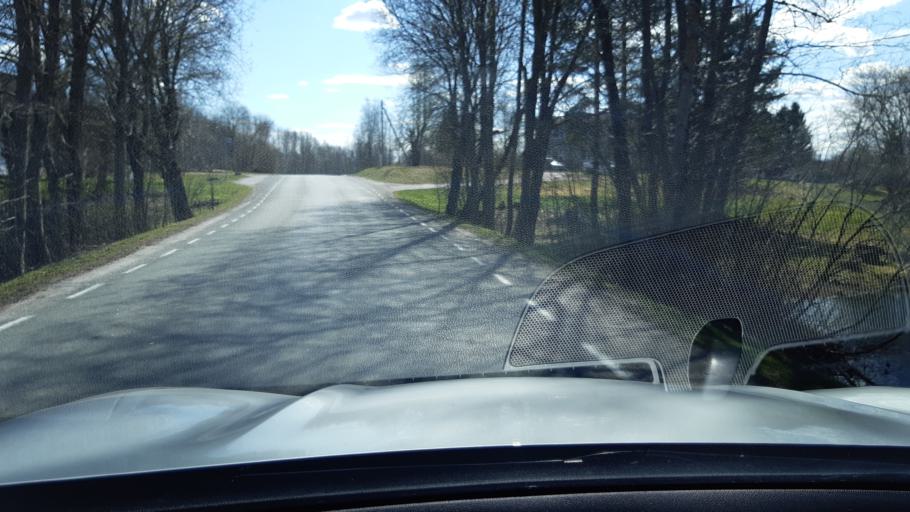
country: EE
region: Raplamaa
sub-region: Kohila vald
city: Kohila
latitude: 59.1809
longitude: 24.8529
